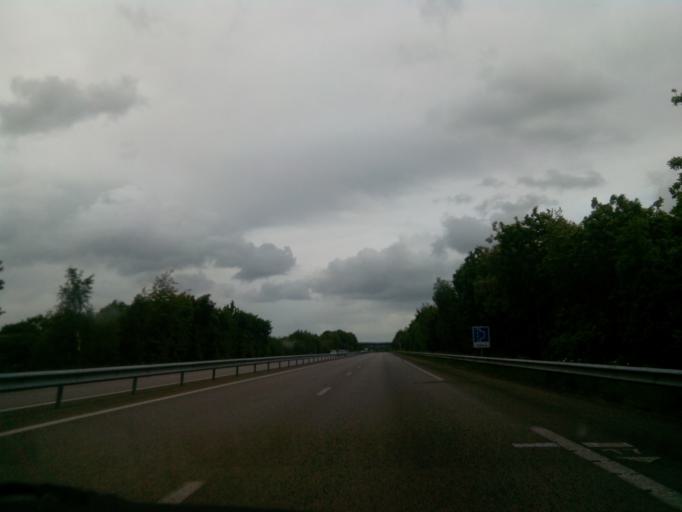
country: FR
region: Brittany
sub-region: Departement du Morbihan
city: Campeneac
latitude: 47.9295
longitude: -2.3255
